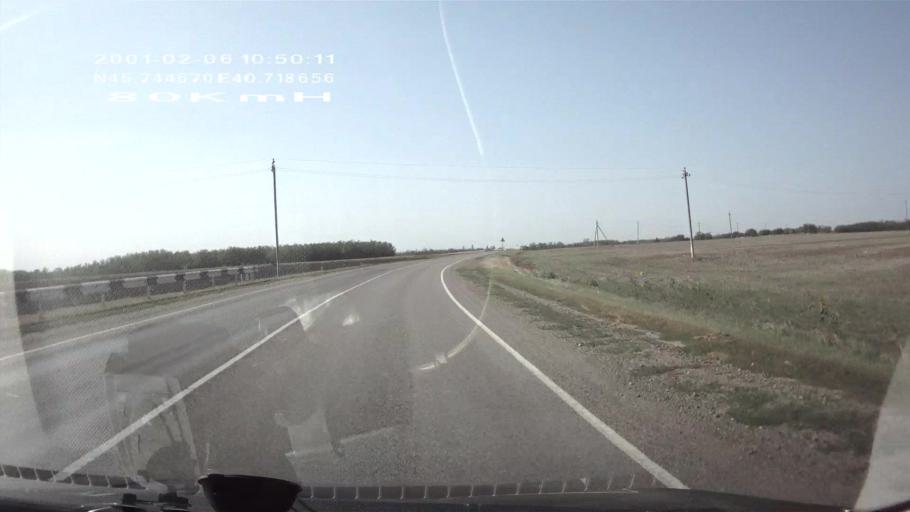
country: RU
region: Krasnodarskiy
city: Dmitriyevskaya
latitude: 45.7442
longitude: 40.7180
